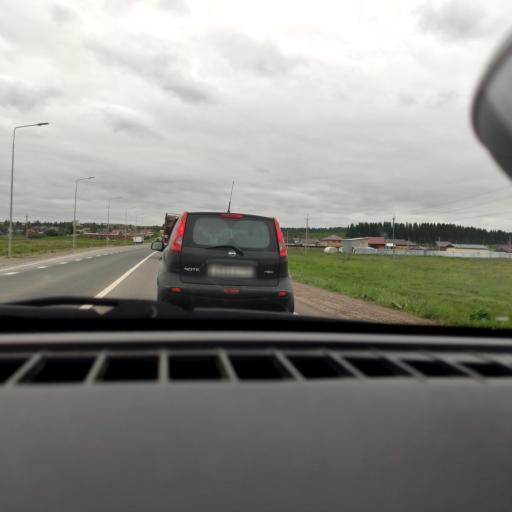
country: RU
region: Perm
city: Kultayevo
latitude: 57.8727
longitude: 55.8634
